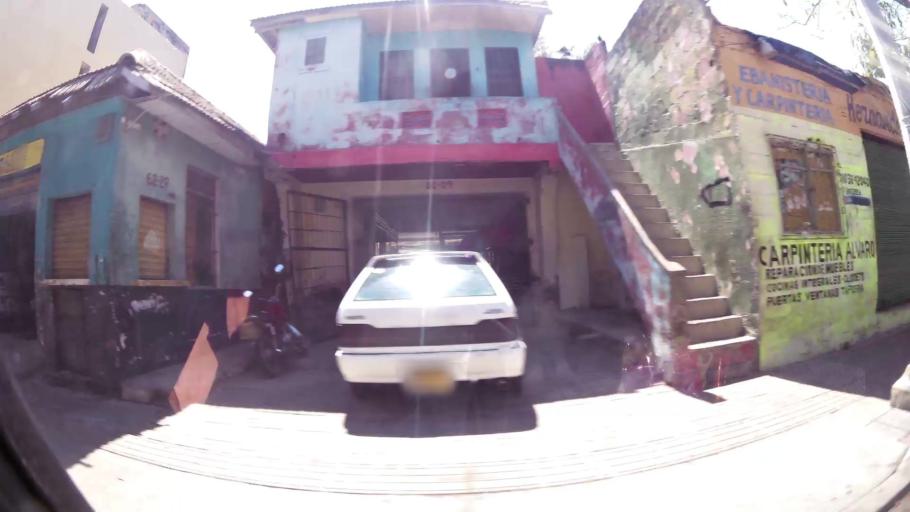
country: CO
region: Atlantico
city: Barranquilla
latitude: 10.9907
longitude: -74.7974
